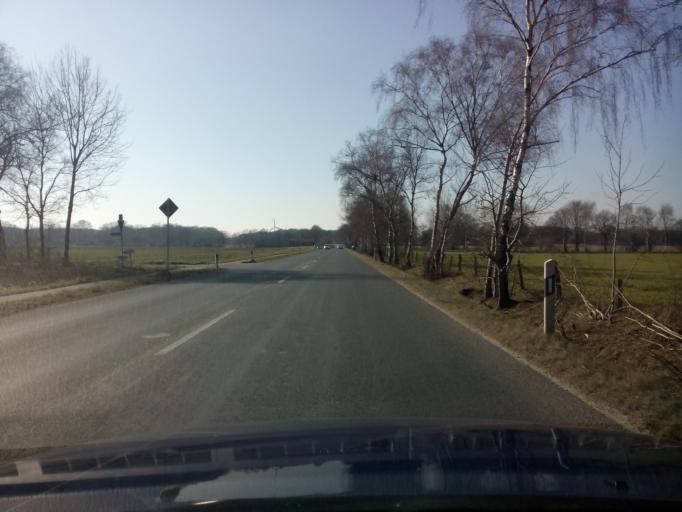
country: DE
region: Lower Saxony
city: Ritterhude
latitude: 53.2303
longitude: 8.6798
